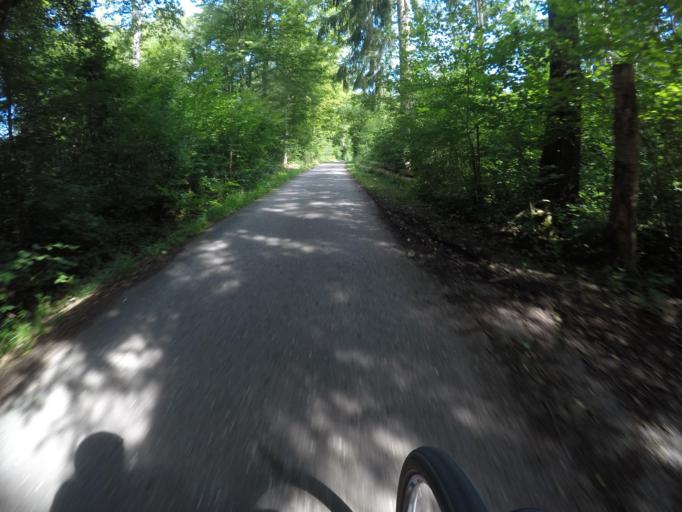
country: DE
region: Baden-Wuerttemberg
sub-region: Karlsruhe Region
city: Otisheim
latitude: 48.9762
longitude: 8.7957
